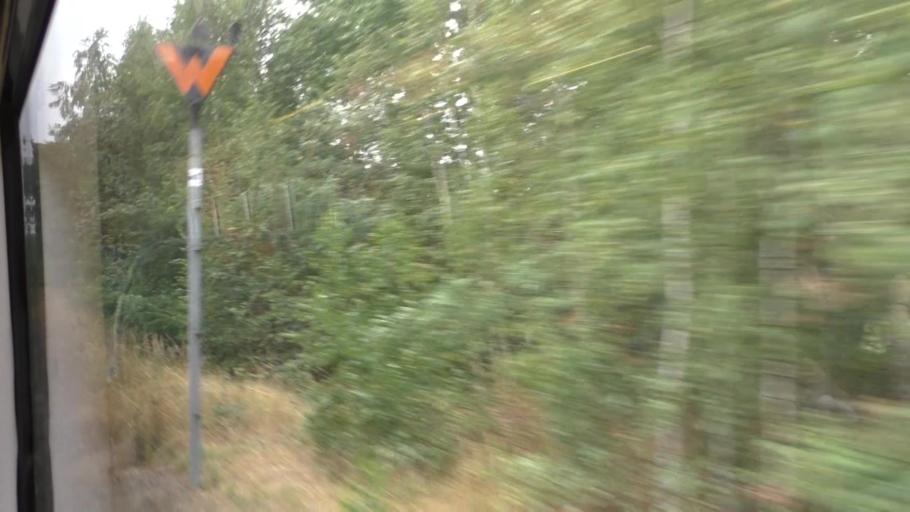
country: DE
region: Saxony
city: Ostritz
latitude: 51.0761
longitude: 14.9636
